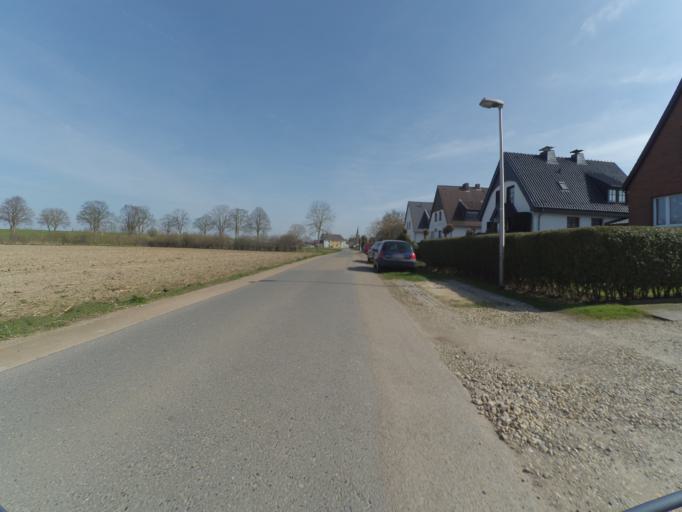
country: DE
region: North Rhine-Westphalia
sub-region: Regierungsbezirk Dusseldorf
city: Kleve
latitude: 51.8304
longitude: 6.0991
